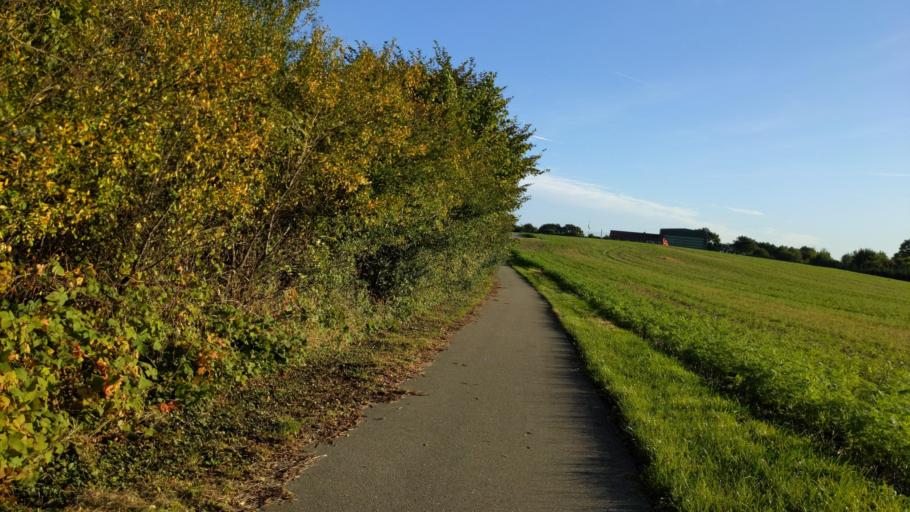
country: DE
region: Schleswig-Holstein
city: Ahrensbok
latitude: 54.0373
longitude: 10.5622
